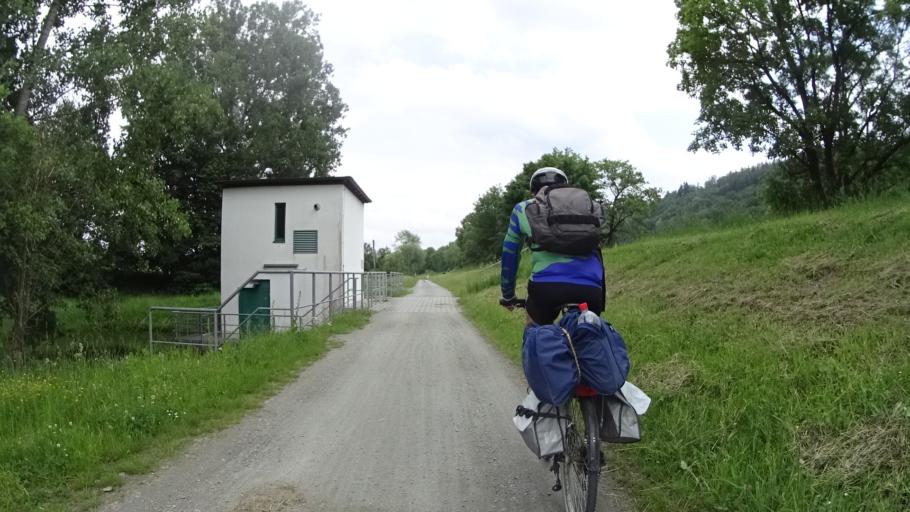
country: DE
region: Bavaria
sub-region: Lower Bavaria
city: Aicha vorm Wald
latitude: 48.6057
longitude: 13.3136
